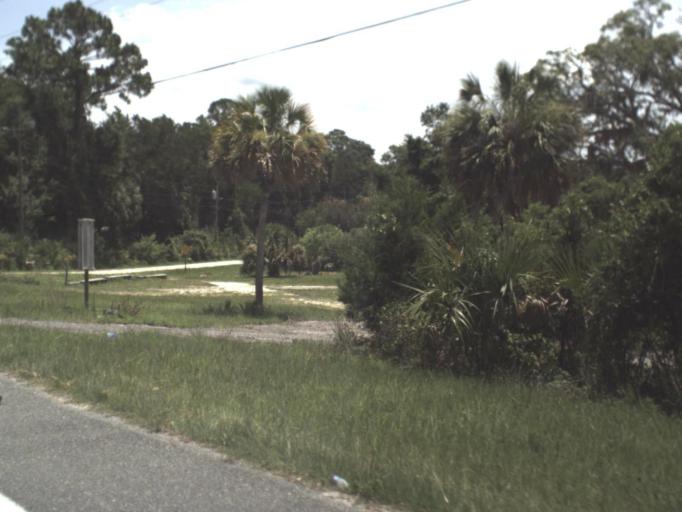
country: US
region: Florida
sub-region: Taylor County
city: Steinhatchee
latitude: 29.6831
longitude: -83.3624
